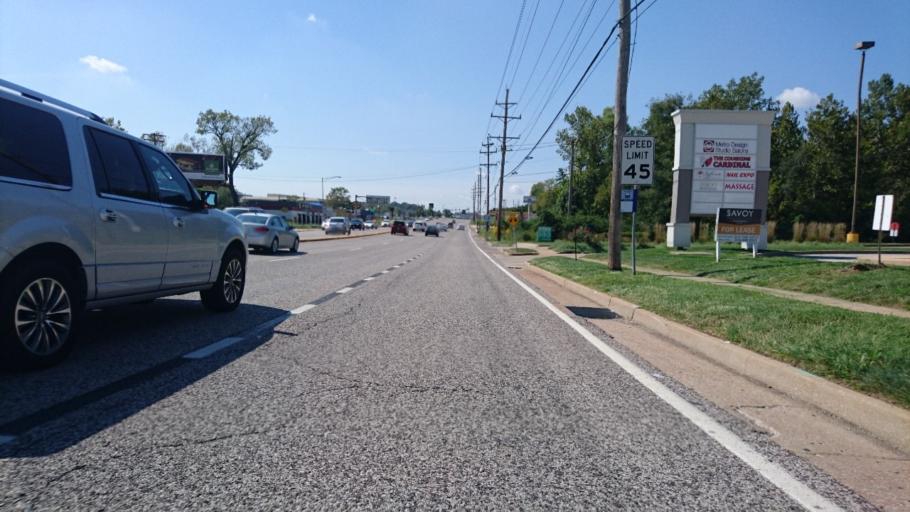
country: US
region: Missouri
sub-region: Saint Louis County
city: Town and Country
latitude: 38.5968
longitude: -90.4747
